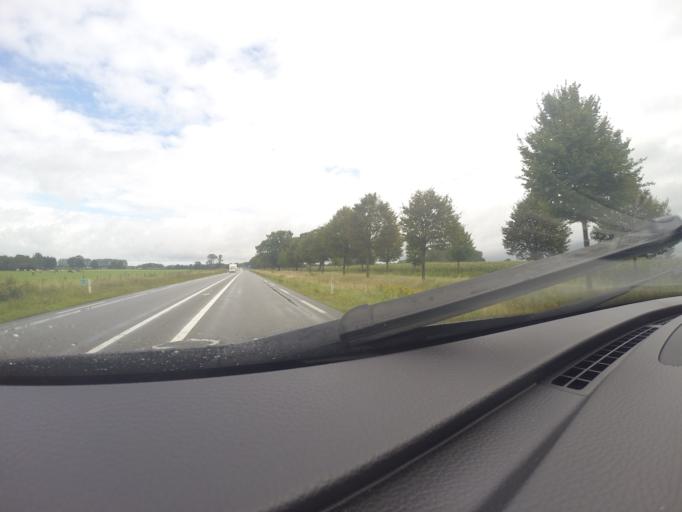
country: NL
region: Gelderland
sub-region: Gemeente Lochem
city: Laren
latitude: 52.2611
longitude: 6.4012
